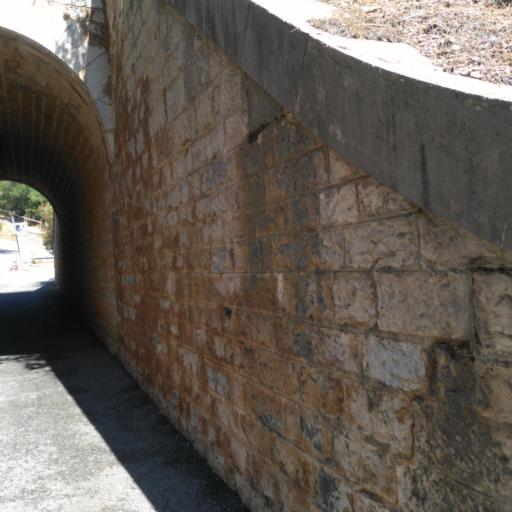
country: FR
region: Provence-Alpes-Cote d'Azur
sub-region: Departement du Var
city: Bandol
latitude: 43.1411
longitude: 5.7460
